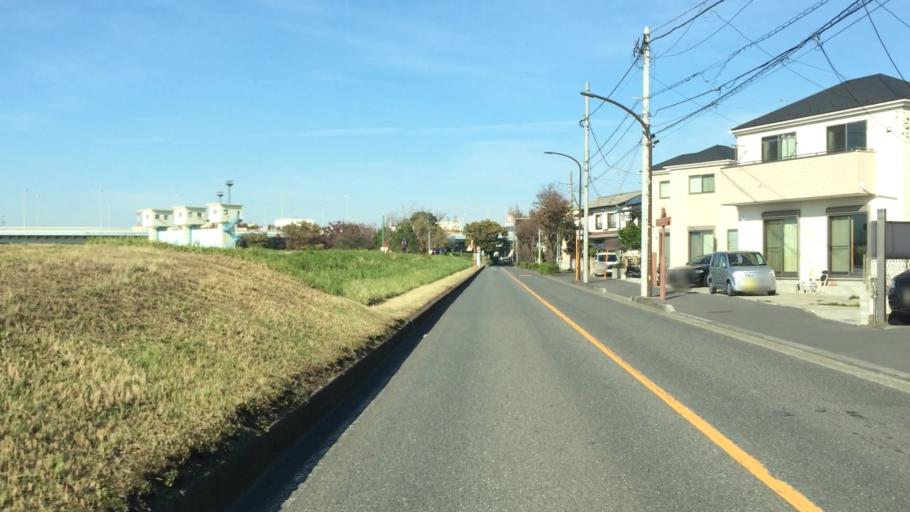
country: JP
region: Tokyo
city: Chofugaoka
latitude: 35.6534
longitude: 139.5152
